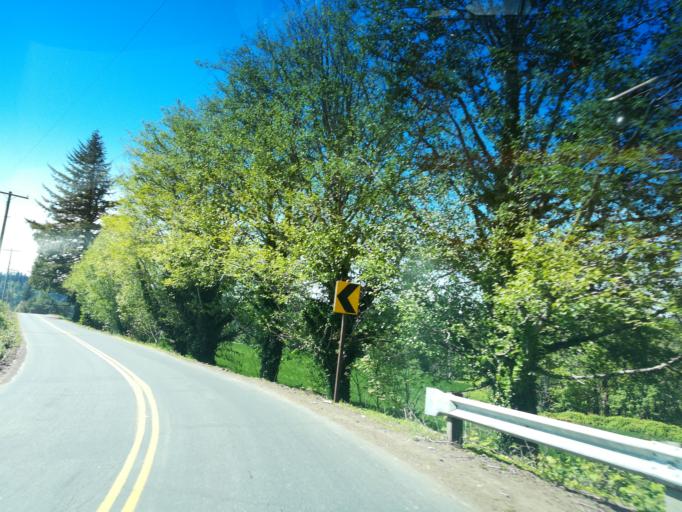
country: US
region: Oregon
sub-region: Multnomah County
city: Troutdale
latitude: 45.5119
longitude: -122.3523
